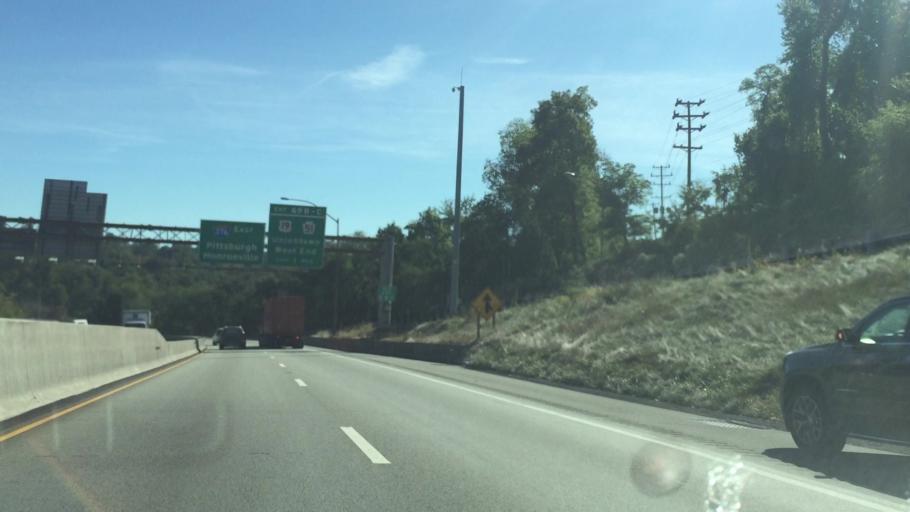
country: US
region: Pennsylvania
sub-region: Allegheny County
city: Green Tree
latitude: 40.4201
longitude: -80.0362
